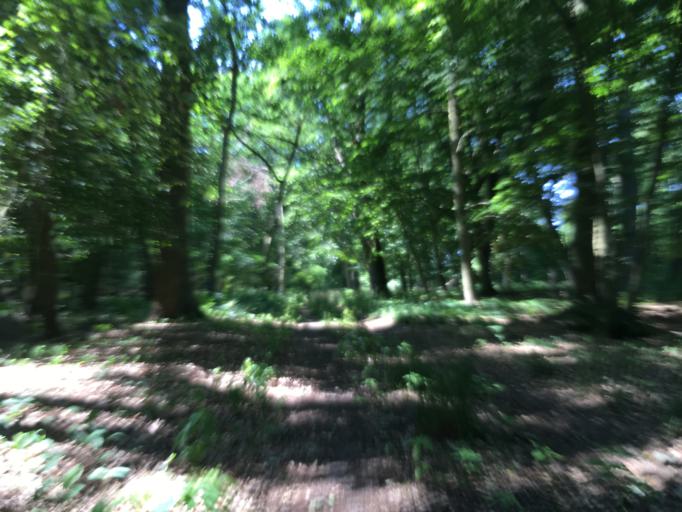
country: DE
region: Brandenburg
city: Zichow
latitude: 53.2346
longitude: 14.1072
